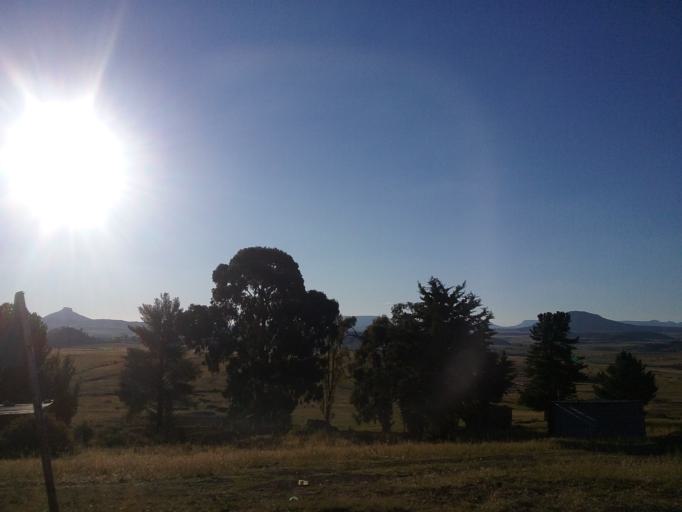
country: LS
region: Mohale's Hoek District
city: Mohale's Hoek
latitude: -30.1826
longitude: 27.4258
